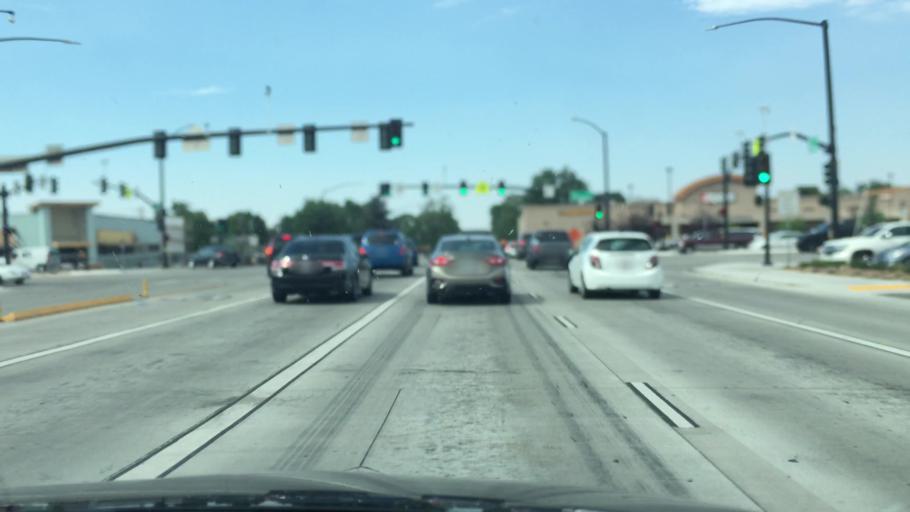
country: US
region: Idaho
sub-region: Ada County
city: Garden City
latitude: 43.6188
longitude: -116.2742
